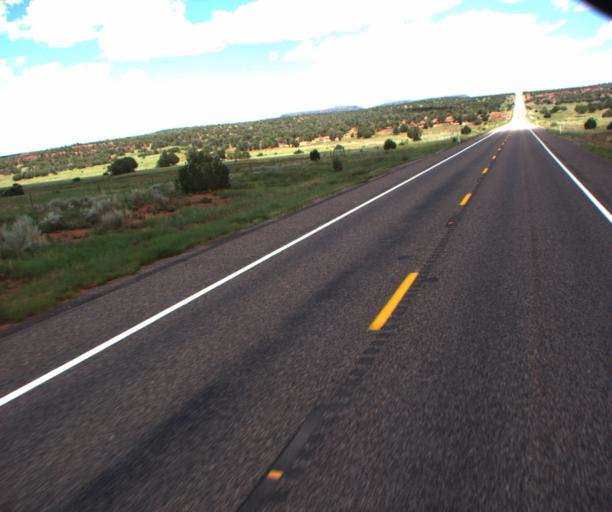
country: US
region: Arizona
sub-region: Apache County
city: Springerville
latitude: 34.1561
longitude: -109.1248
